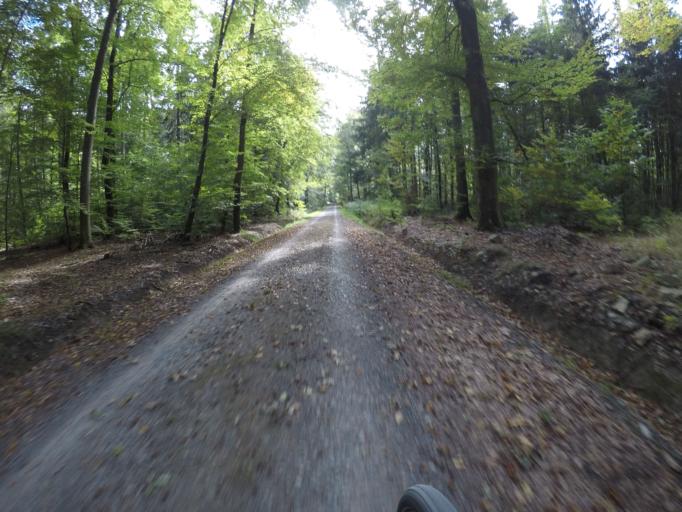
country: DE
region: Baden-Wuerttemberg
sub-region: Regierungsbezirk Stuttgart
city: Hildrizhausen
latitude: 48.6108
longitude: 8.9330
